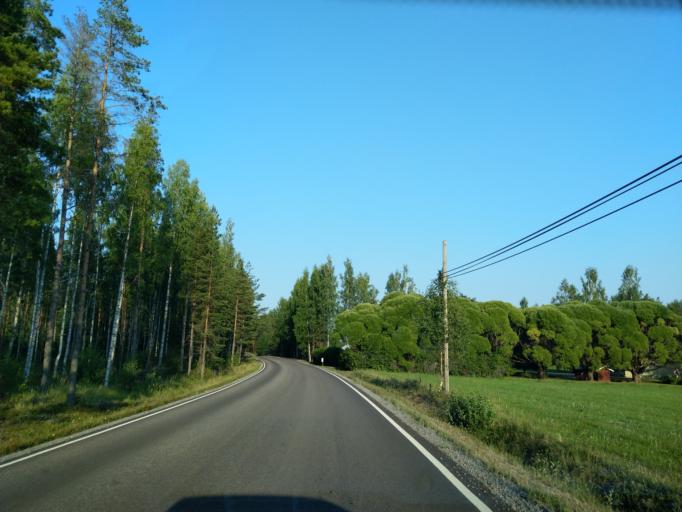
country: FI
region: Satakunta
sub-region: Pohjois-Satakunta
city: Honkajoki
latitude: 61.8206
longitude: 22.2184
